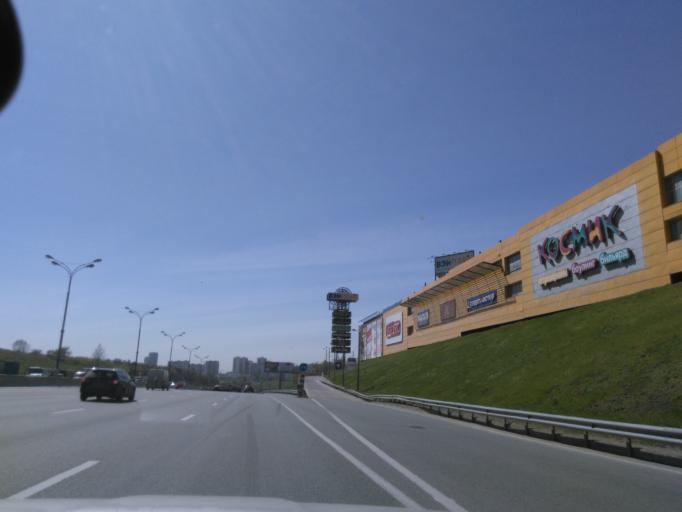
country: RU
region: Moscow
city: Strogino
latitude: 55.8585
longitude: 37.3970
